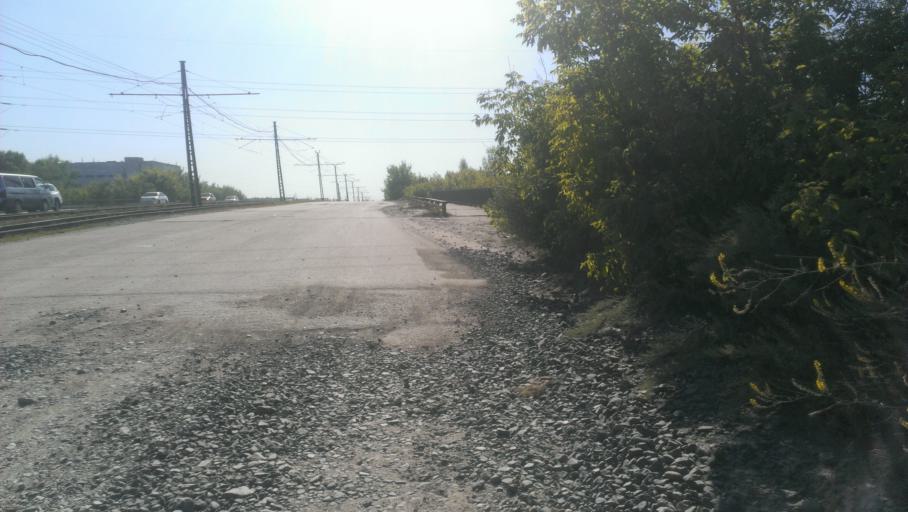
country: RU
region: Altai Krai
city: Novosilikatnyy
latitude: 53.3256
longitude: 83.6496
